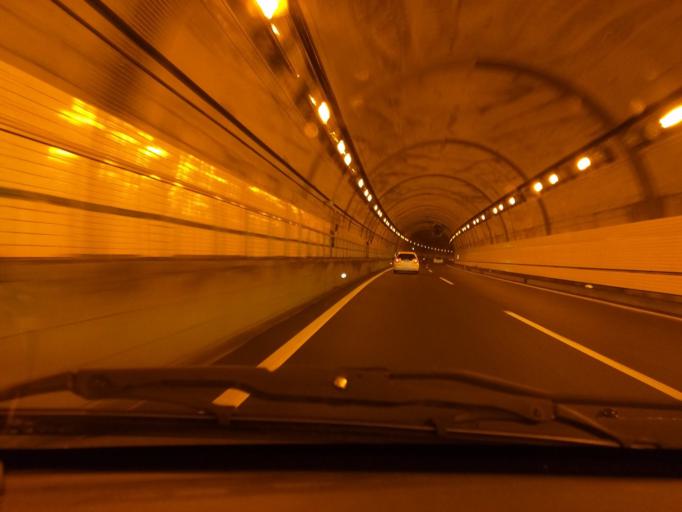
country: JP
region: Niigata
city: Kashiwazaki
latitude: 37.3203
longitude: 138.4561
